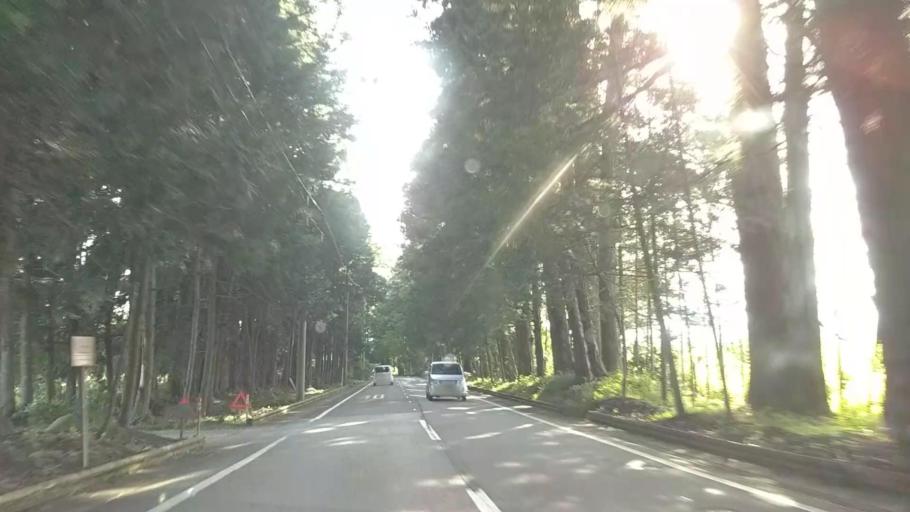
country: JP
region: Tochigi
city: Imaichi
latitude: 36.7373
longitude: 139.6973
